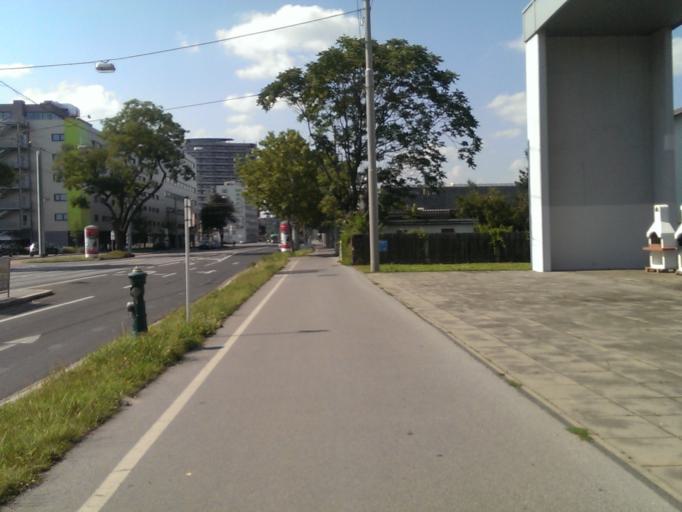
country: AT
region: Styria
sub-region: Graz Stadt
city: Graz
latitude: 47.0541
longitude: 15.4489
